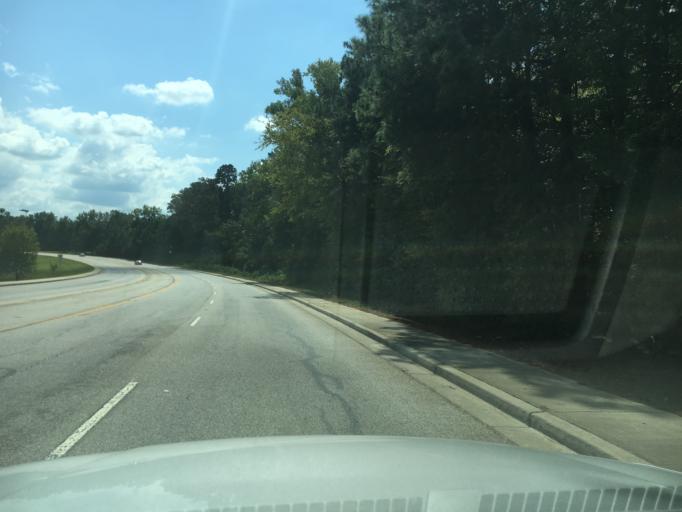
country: US
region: South Carolina
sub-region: Greenwood County
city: Greenwood
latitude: 34.2127
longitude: -82.2057
